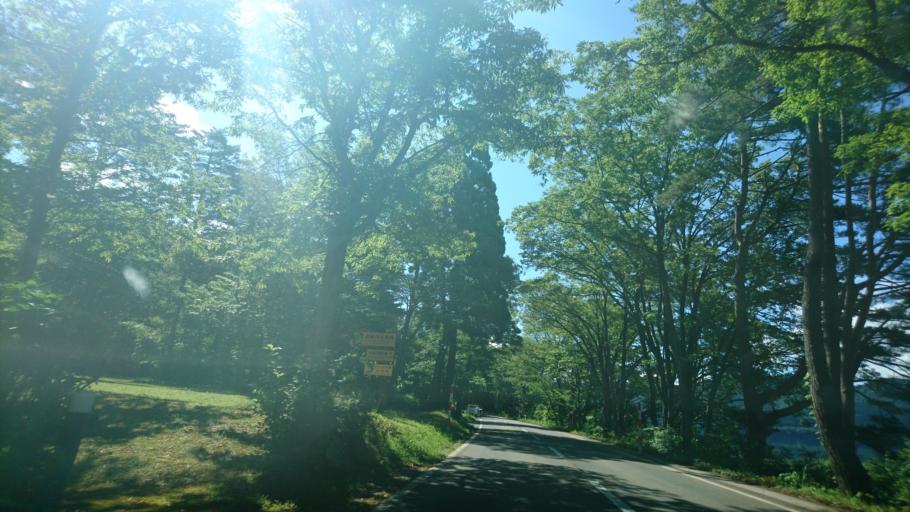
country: JP
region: Akita
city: Kakunodatemachi
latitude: 39.7424
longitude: 140.6870
